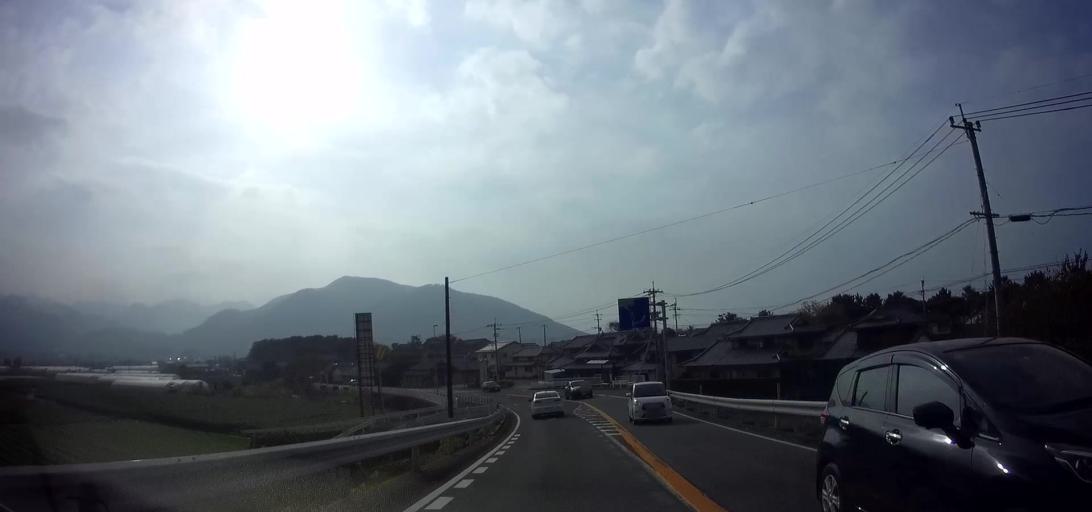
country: JP
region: Nagasaki
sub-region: Isahaya-shi
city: Isahaya
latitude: 32.7939
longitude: 130.1834
